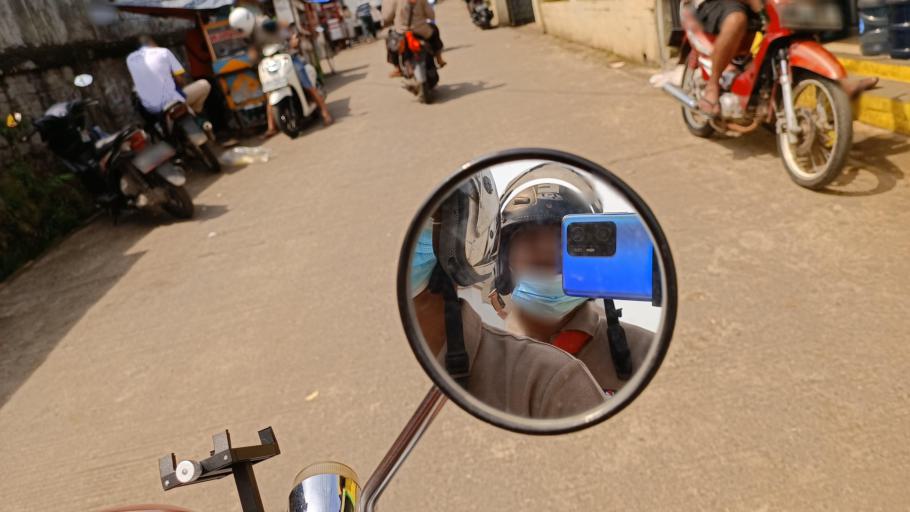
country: ID
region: West Java
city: Caringin
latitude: -6.6522
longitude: 106.8929
